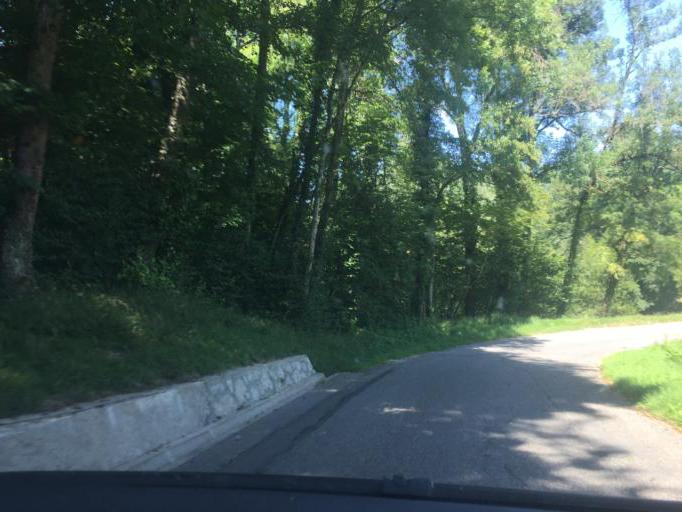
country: FR
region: Rhone-Alpes
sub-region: Departement de la Haute-Savoie
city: Sillingy
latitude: 45.9297
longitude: 6.0001
